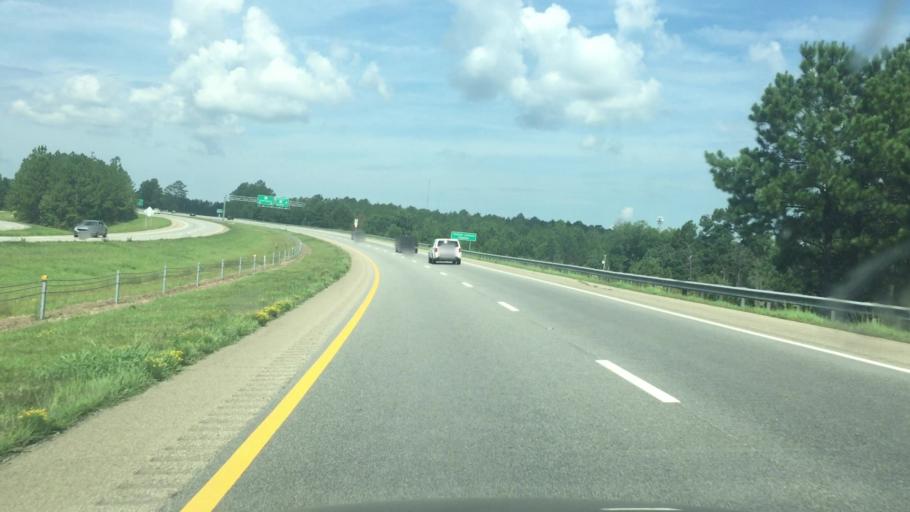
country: US
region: North Carolina
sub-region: Richmond County
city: Hamlet
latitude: 34.8680
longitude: -79.6429
